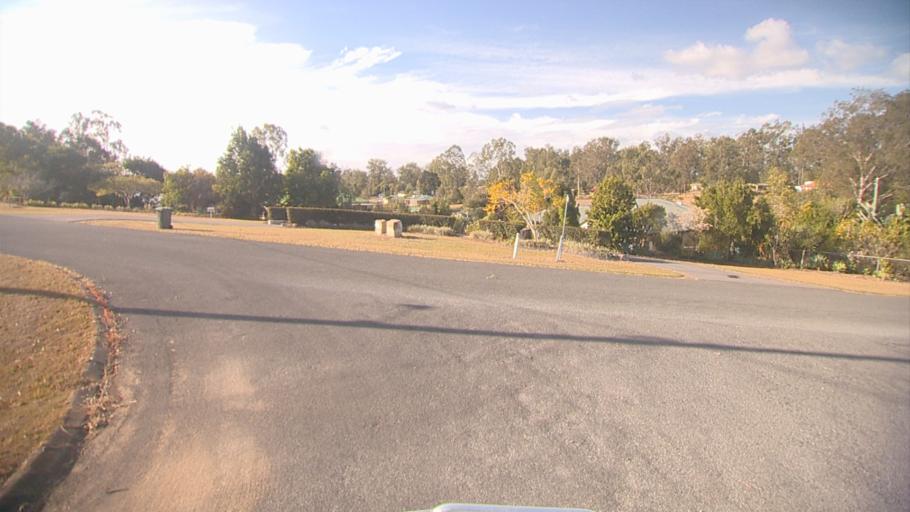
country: AU
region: Queensland
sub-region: Logan
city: Cedar Vale
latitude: -27.8756
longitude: 153.0067
